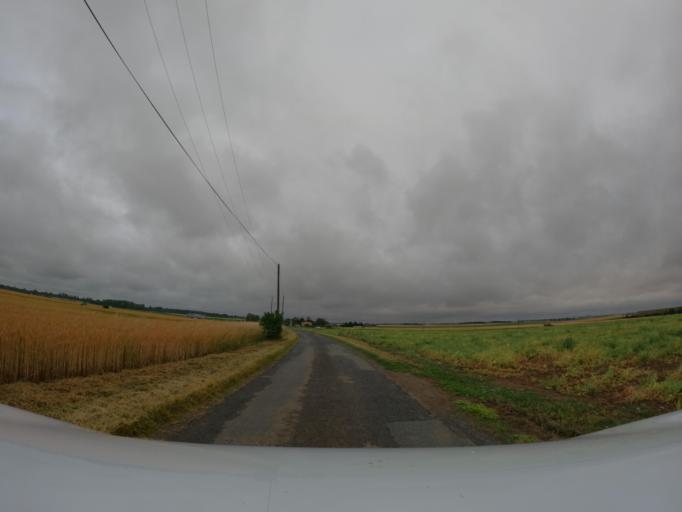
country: FR
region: Pays de la Loire
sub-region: Departement de la Vendee
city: Maillezais
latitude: 46.4027
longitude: -0.7193
